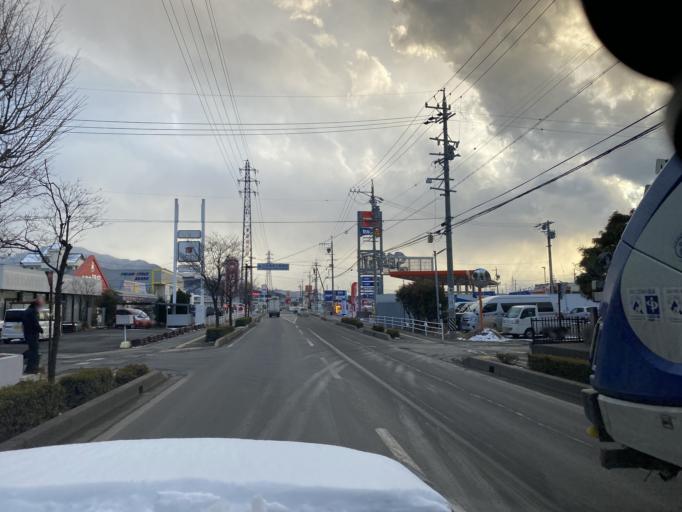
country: JP
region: Nagano
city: Nagano-shi
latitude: 36.6321
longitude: 138.2392
